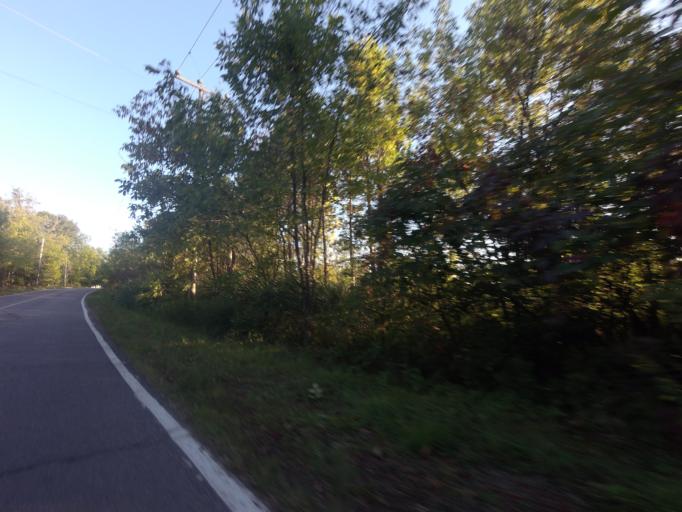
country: CA
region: Quebec
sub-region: Monteregie
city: Hudson
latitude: 45.4794
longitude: -74.2027
